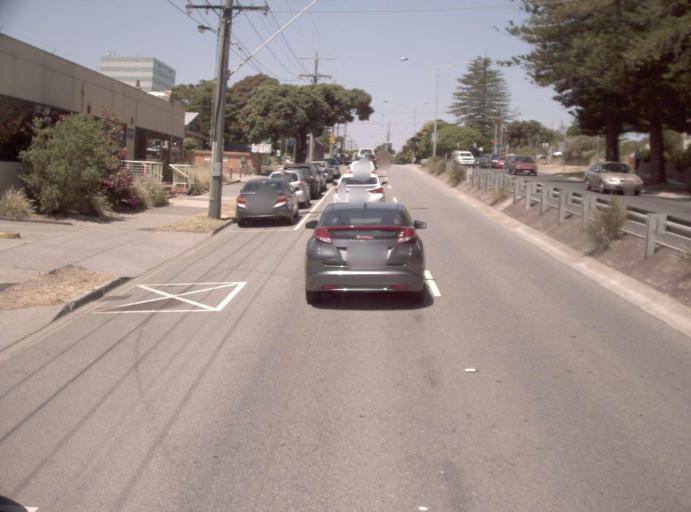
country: AU
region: Victoria
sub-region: Frankston
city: Frankston
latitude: -38.1456
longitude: 145.1210
